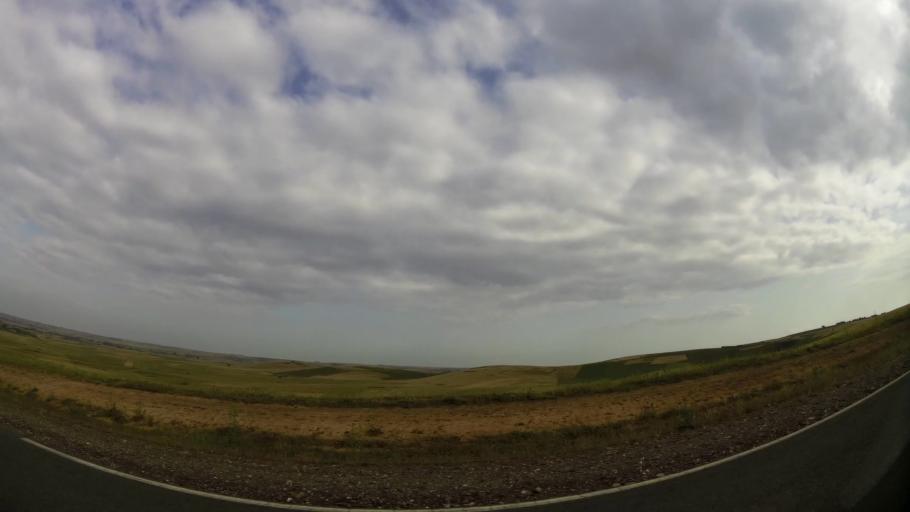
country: MA
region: Rabat-Sale-Zemmour-Zaer
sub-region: Khemisset
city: Khemisset
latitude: 33.7722
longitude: -6.1580
